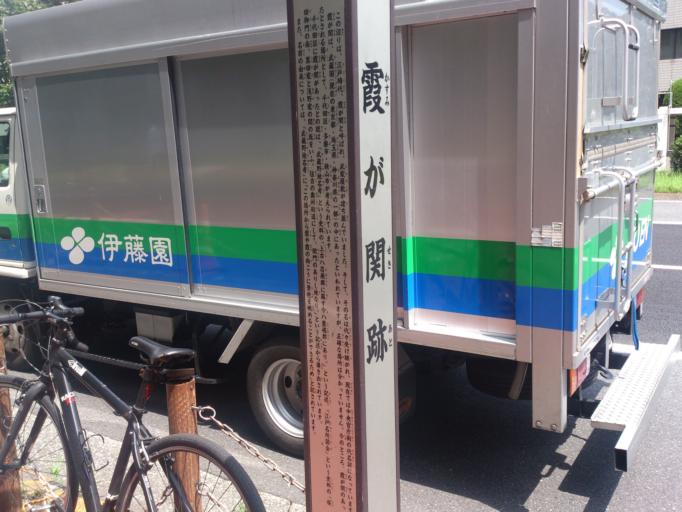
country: JP
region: Tokyo
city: Tokyo
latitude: 35.6750
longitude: 139.7515
